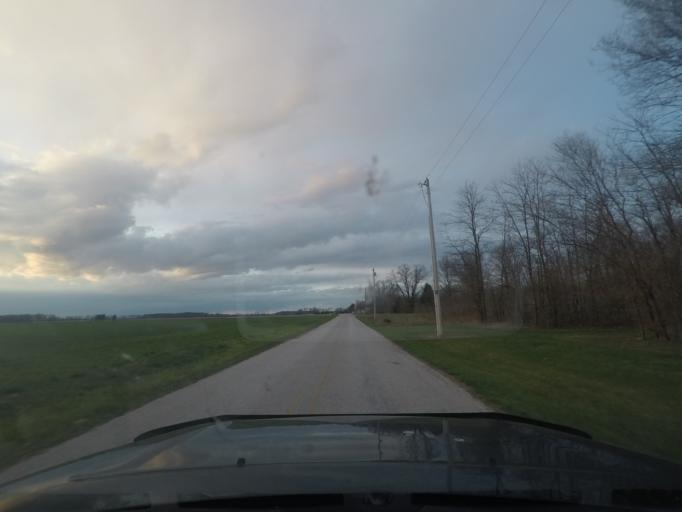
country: US
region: Indiana
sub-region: LaPorte County
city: Kingsford Heights
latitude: 41.4751
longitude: -86.7006
